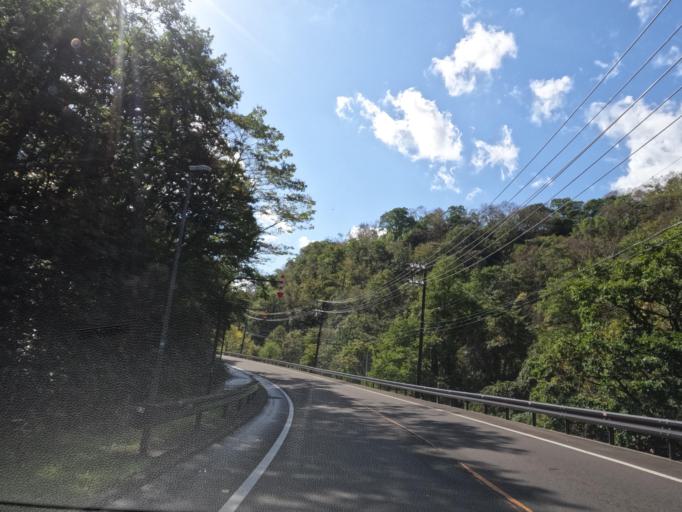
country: JP
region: Hokkaido
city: Shiraoi
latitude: 42.4853
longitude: 141.1449
